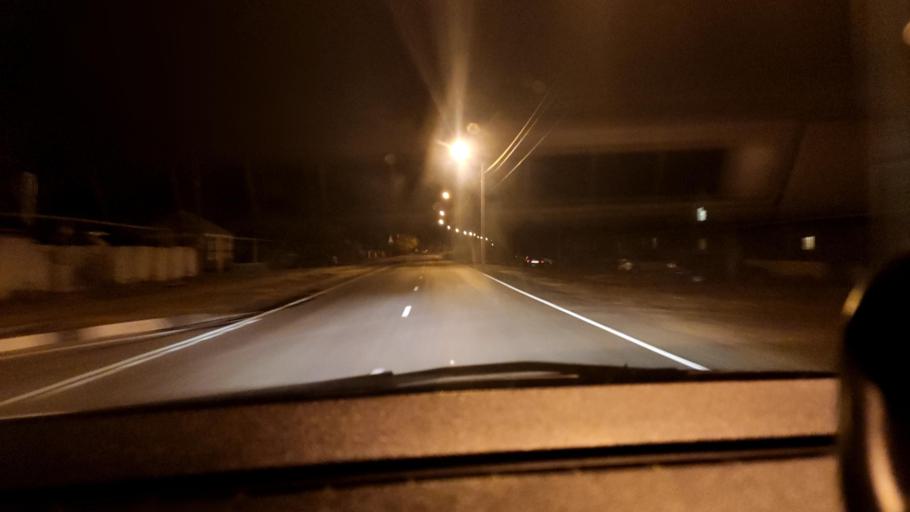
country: RU
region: Voronezj
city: Shilovo
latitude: 51.5616
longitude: 39.0566
